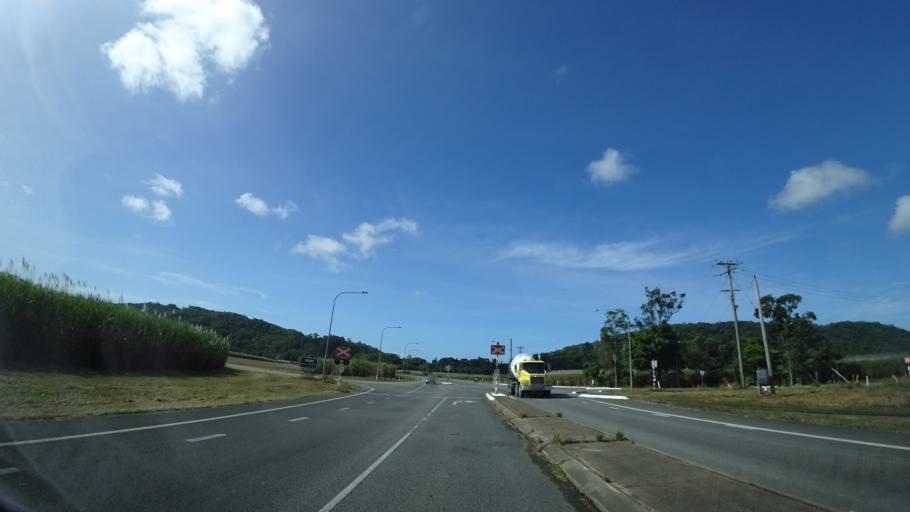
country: AU
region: Queensland
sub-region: Cairns
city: Port Douglas
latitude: -16.4825
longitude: 145.3900
